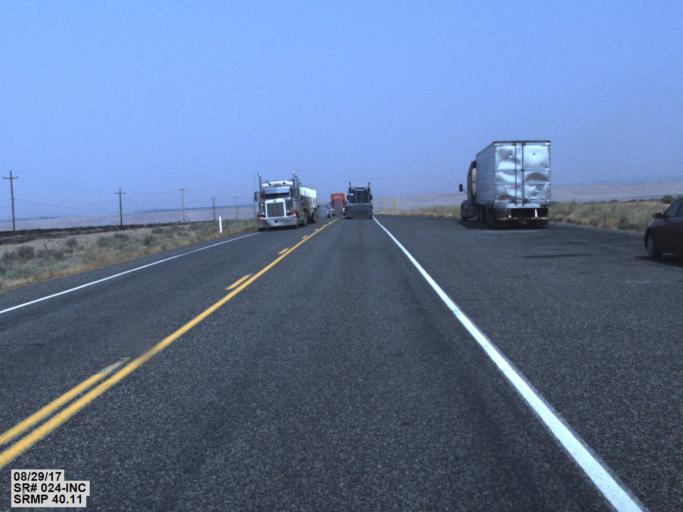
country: US
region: Washington
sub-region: Grant County
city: Desert Aire
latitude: 46.5976
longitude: -119.7274
